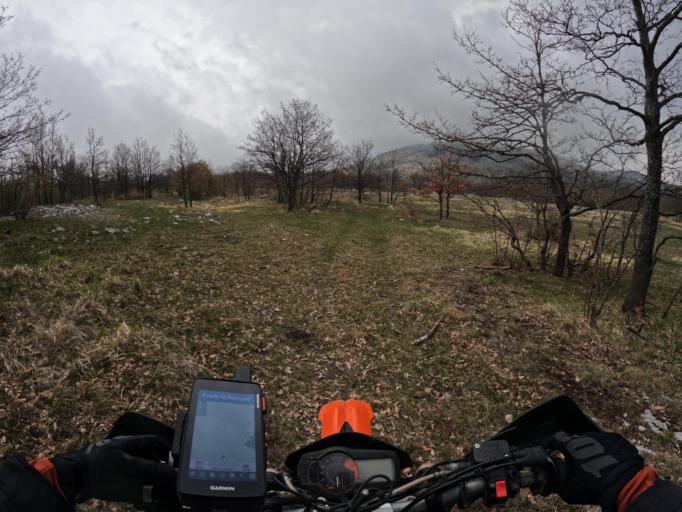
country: HR
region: Zadarska
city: Gracac
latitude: 44.3907
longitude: 15.9751
